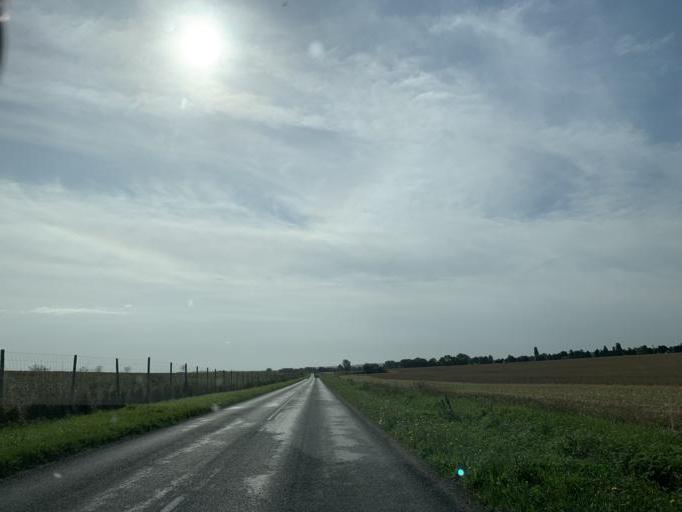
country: FR
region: Ile-de-France
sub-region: Departement de Seine-et-Marne
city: Annet-sur-Marne
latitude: 48.9355
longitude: 2.7072
